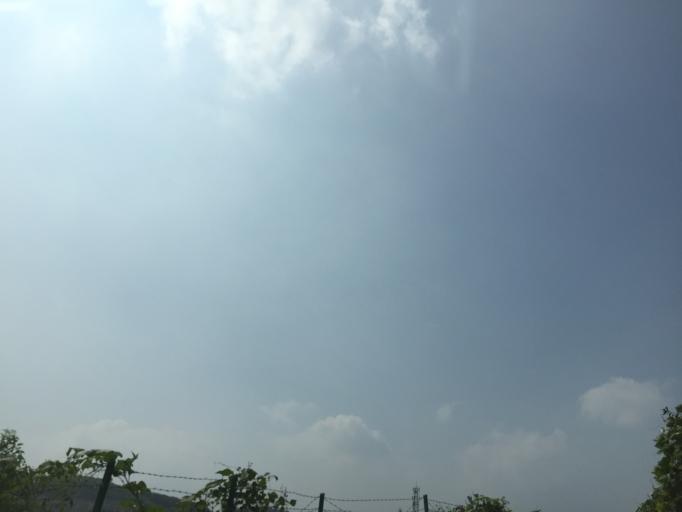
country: CN
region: Guizhou Sheng
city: Qinglong
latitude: 28.2948
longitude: 108.1116
